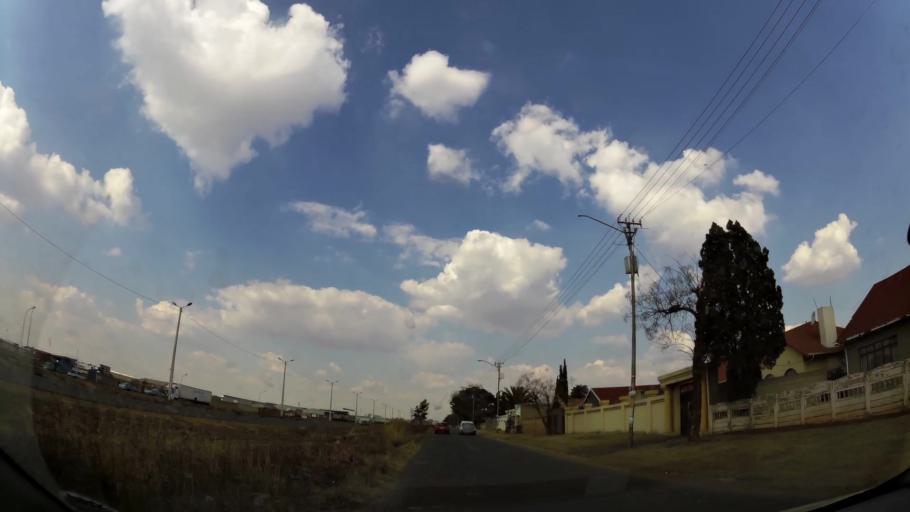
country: ZA
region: Gauteng
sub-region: Ekurhuleni Metropolitan Municipality
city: Germiston
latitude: -26.3063
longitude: 28.1945
